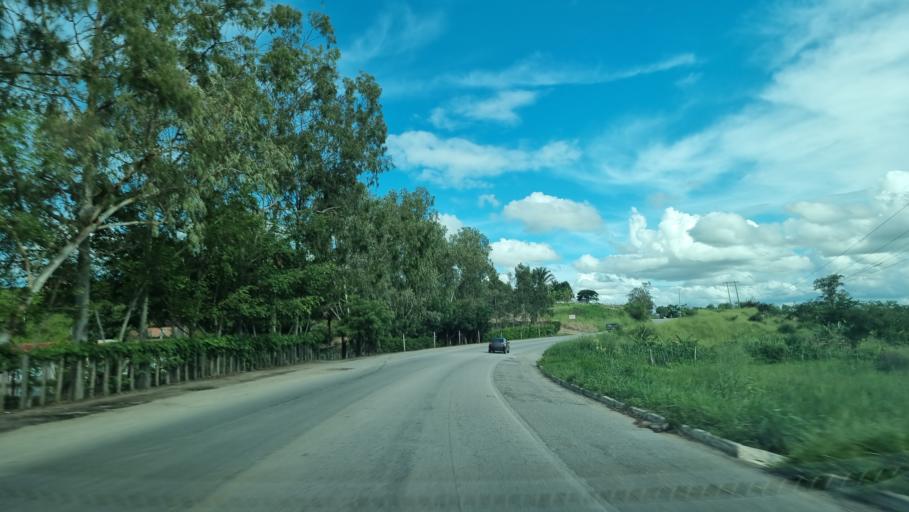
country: BR
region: Pernambuco
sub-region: Caruaru
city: Caruaru
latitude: -8.3712
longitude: -35.9837
